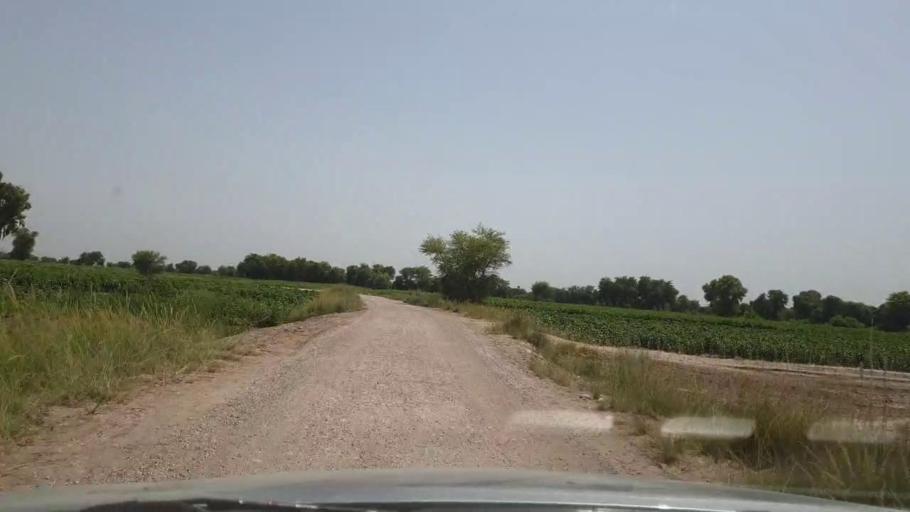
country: PK
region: Sindh
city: Pano Aqil
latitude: 27.7992
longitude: 69.2419
